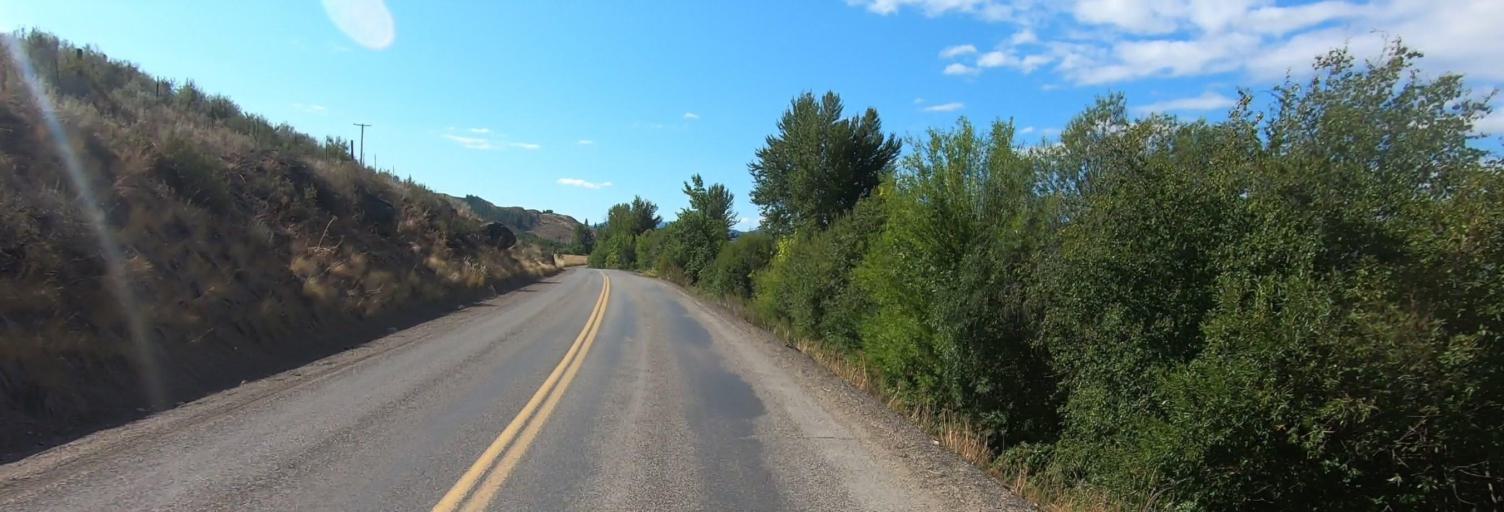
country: US
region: Washington
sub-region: Okanogan County
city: Brewster
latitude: 48.5063
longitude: -120.1762
